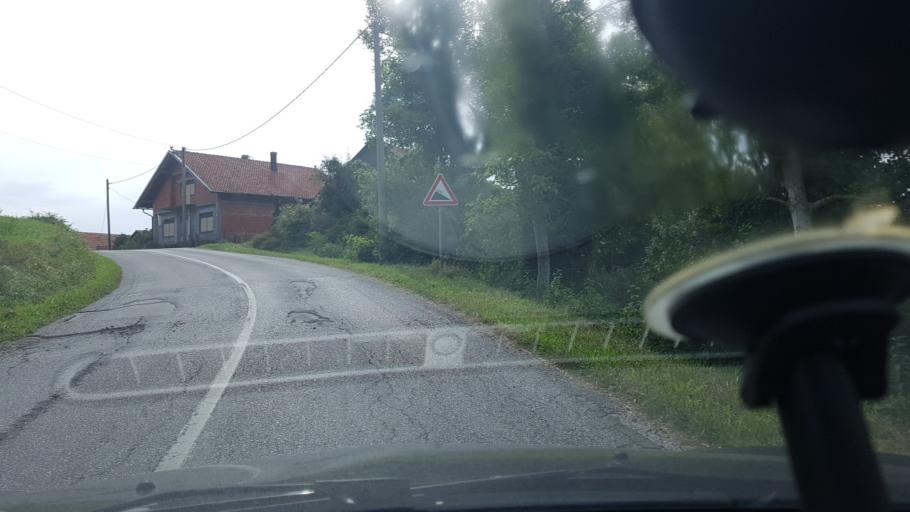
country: HR
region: Varazdinska
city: Ljubescica
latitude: 46.0975
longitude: 16.3428
